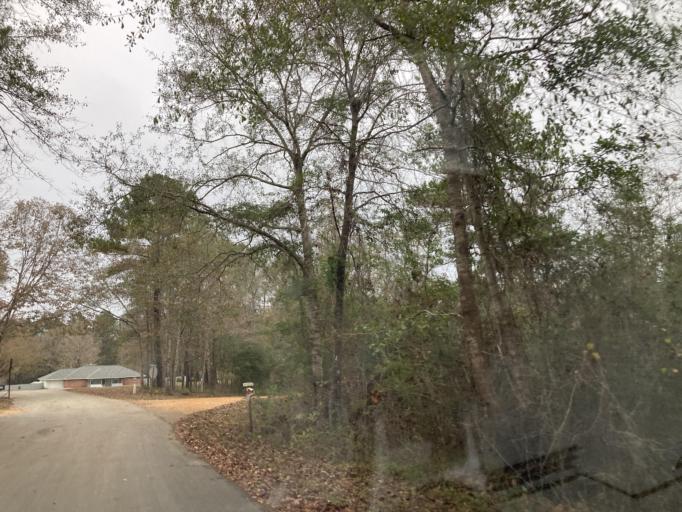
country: US
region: Mississippi
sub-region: Lamar County
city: Purvis
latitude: 31.1975
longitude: -89.4289
